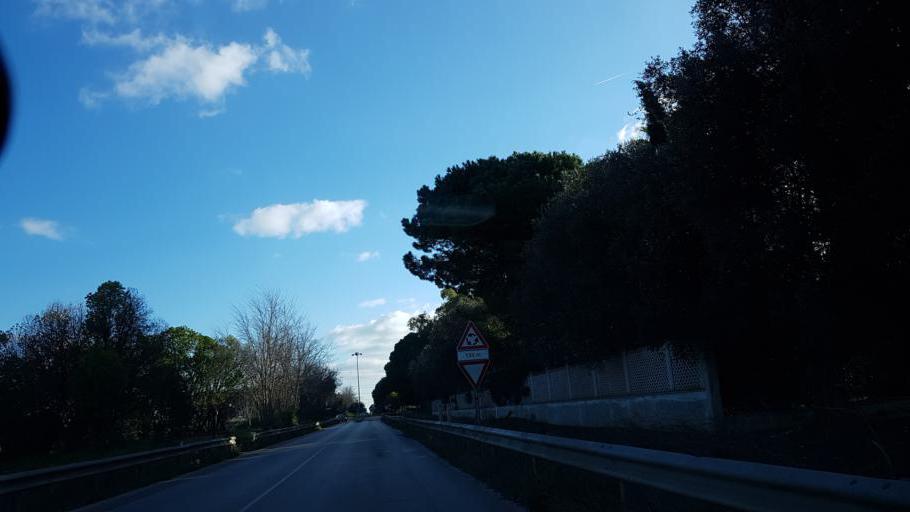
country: IT
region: Apulia
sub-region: Provincia di Brindisi
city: La Rosa
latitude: 40.6111
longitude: 17.9532
